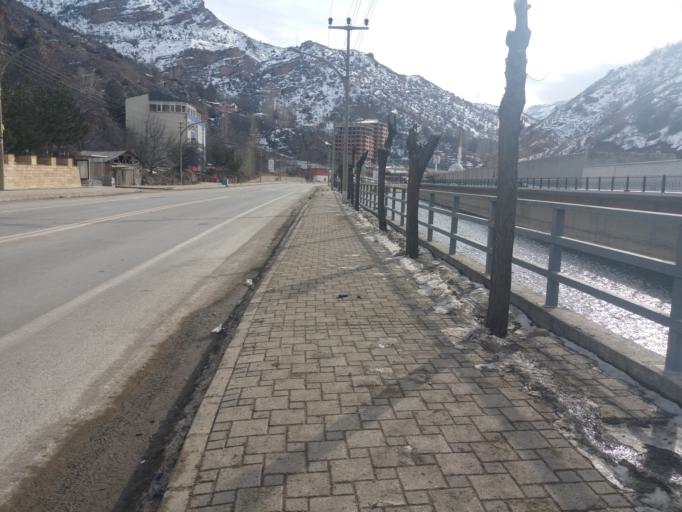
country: TR
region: Gumushane
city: Gumushkhane
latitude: 40.4470
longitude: 39.5015
